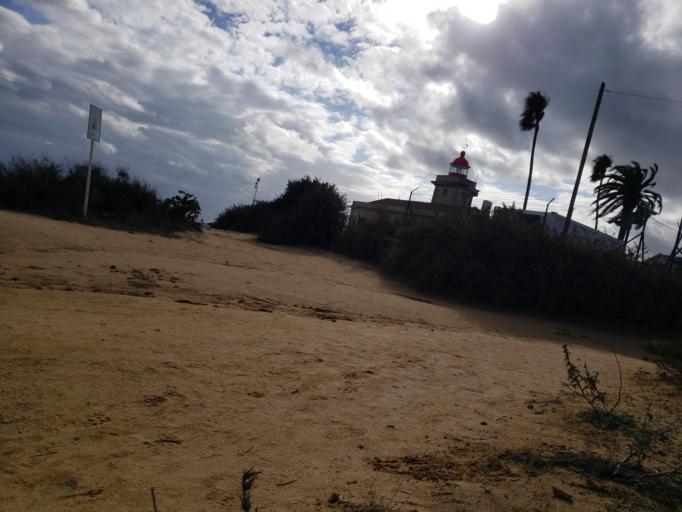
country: PT
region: Faro
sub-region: Lagos
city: Lagos
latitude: 37.0811
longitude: -8.6691
